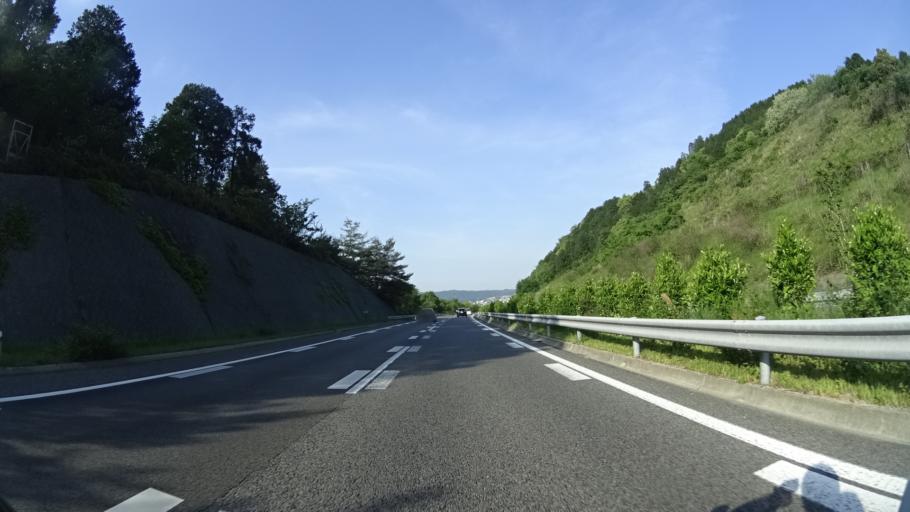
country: JP
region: Ehime
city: Saijo
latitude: 33.9028
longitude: 133.2020
